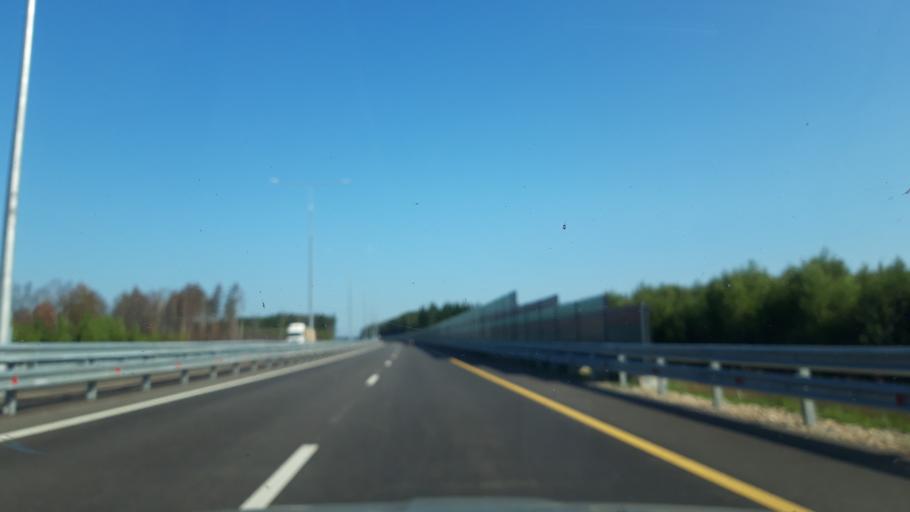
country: RU
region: Moskovskaya
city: Spas-Zaulok
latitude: 56.4798
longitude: 36.5385
